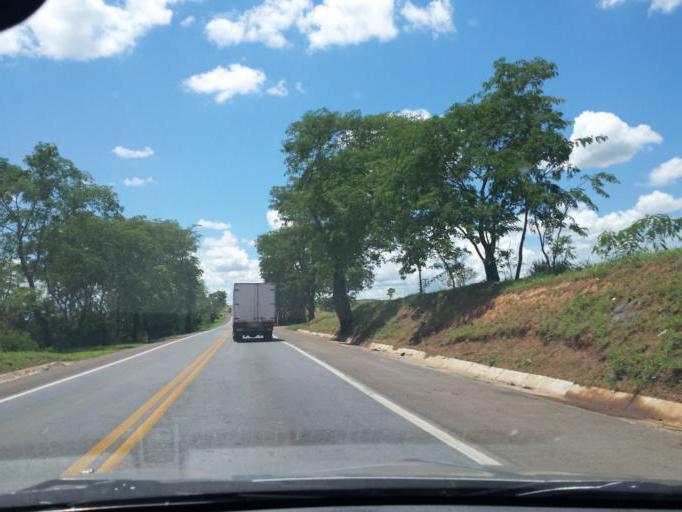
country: BR
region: Goias
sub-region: Cristalina
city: Cristalina
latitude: -16.5989
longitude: -47.7738
